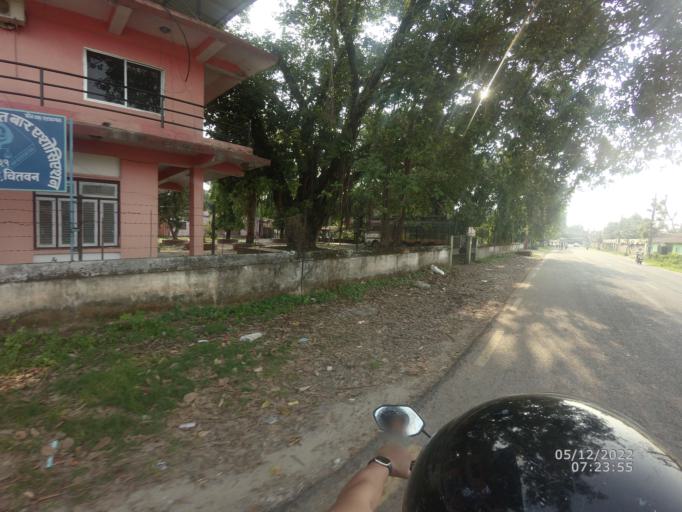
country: NP
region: Central Region
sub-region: Narayani Zone
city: Bharatpur
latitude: 27.6803
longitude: 84.4375
